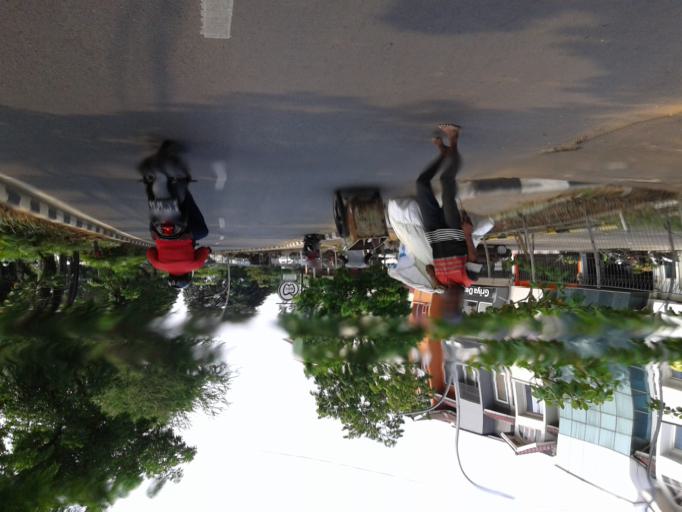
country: ID
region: West Java
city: Pamulang
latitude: -6.3056
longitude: 106.7820
